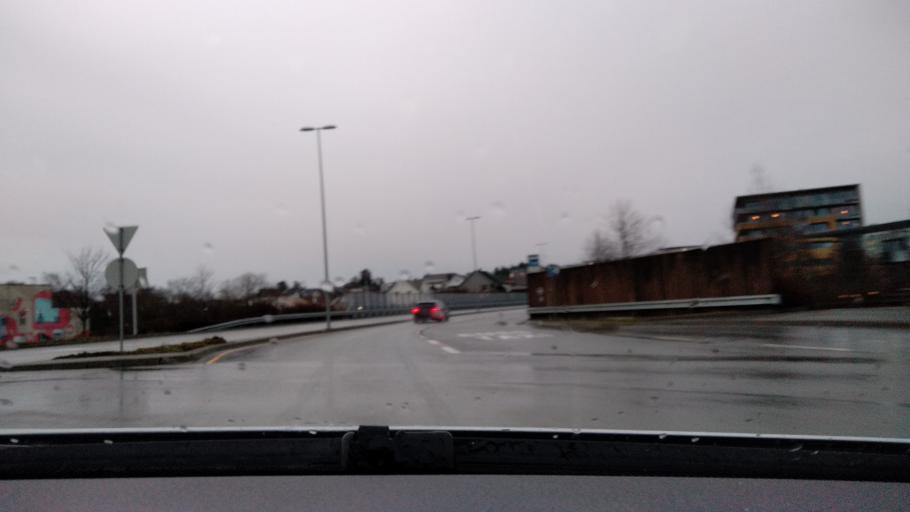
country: NO
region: Rogaland
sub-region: Stavanger
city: Stavanger
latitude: 58.9530
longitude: 5.6715
